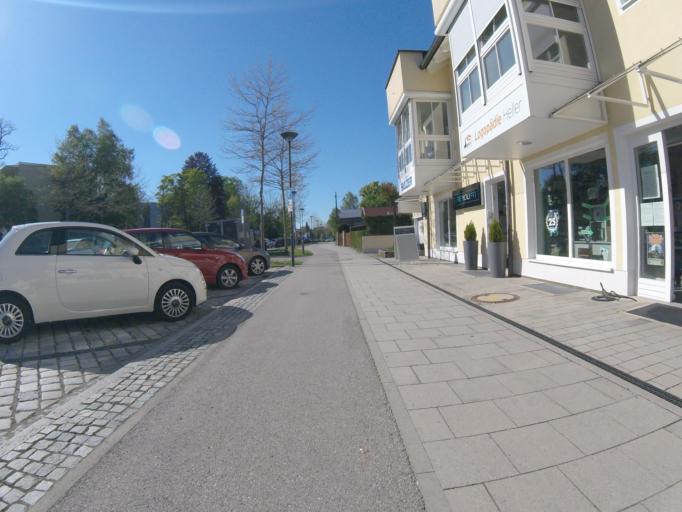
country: DE
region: Bavaria
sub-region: Upper Bavaria
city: Ottobrunn
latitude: 48.0696
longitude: 11.6576
